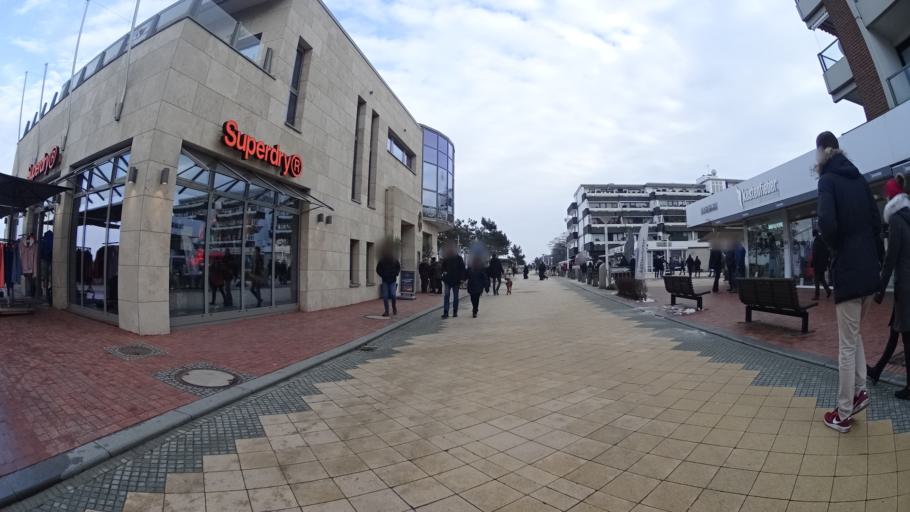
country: DE
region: Schleswig-Holstein
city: Scharbeutz
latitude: 54.0261
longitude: 10.7580
